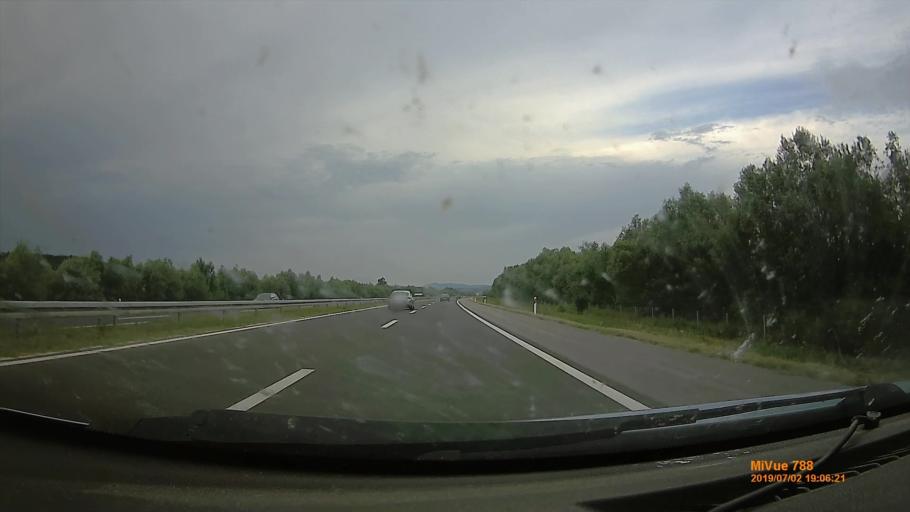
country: HR
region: Varazdinska
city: Remetinec
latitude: 46.0152
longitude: 16.2946
